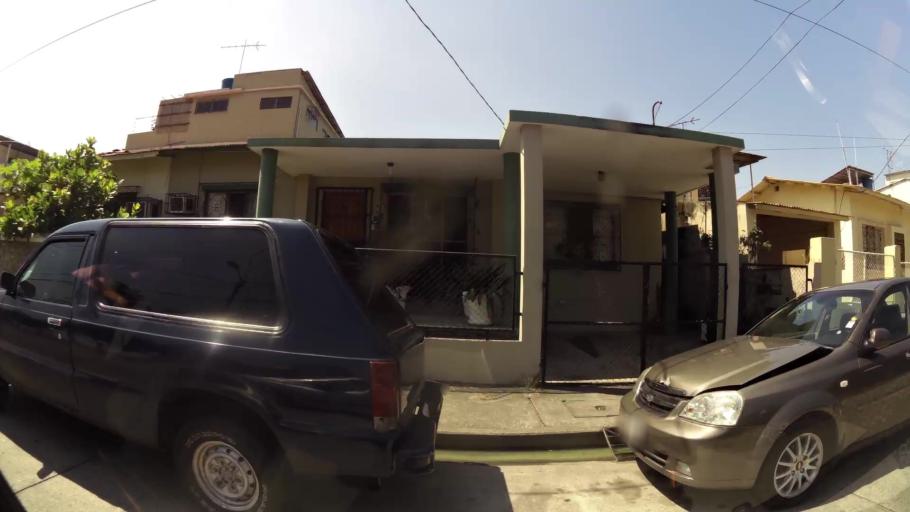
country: EC
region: Guayas
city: Guayaquil
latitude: -2.1612
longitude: -79.9151
